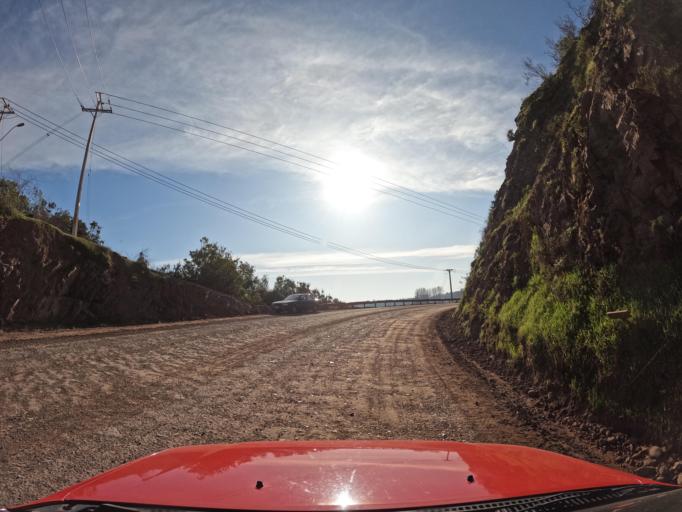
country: CL
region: Maule
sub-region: Provincia de Curico
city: Teno
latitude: -34.9692
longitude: -70.9477
